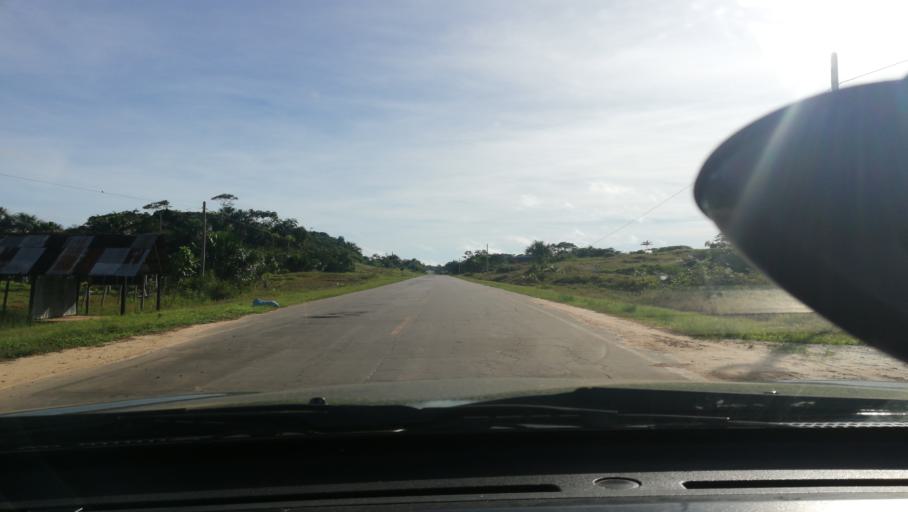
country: PE
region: Loreto
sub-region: Provincia de Loreto
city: Nauta
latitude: -4.3437
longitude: -73.5401
